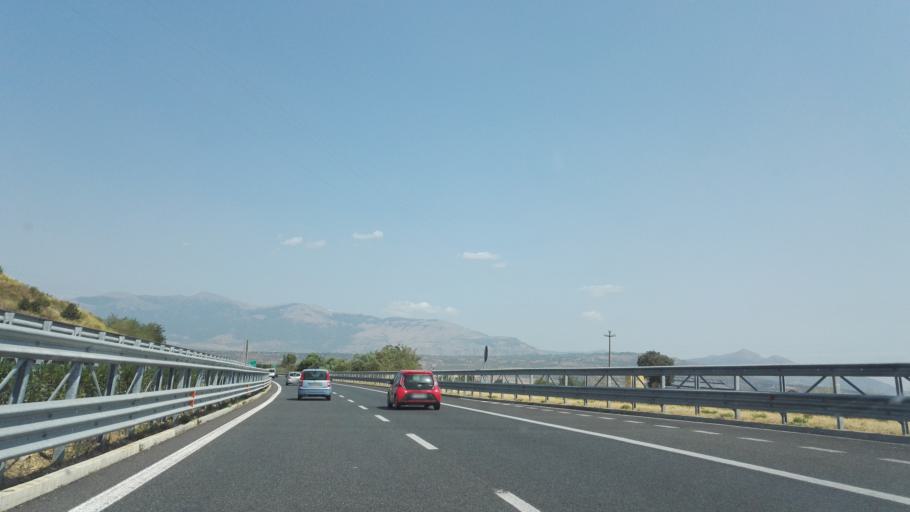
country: IT
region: Calabria
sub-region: Provincia di Cosenza
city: San Lorenzo del Vallo
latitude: 39.7091
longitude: 16.2443
